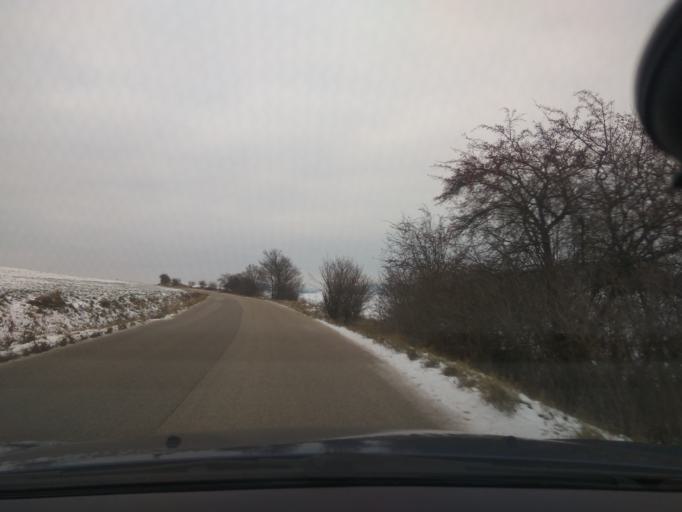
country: SK
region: Nitriansky
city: Stara Tura
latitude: 48.7917
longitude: 17.7309
